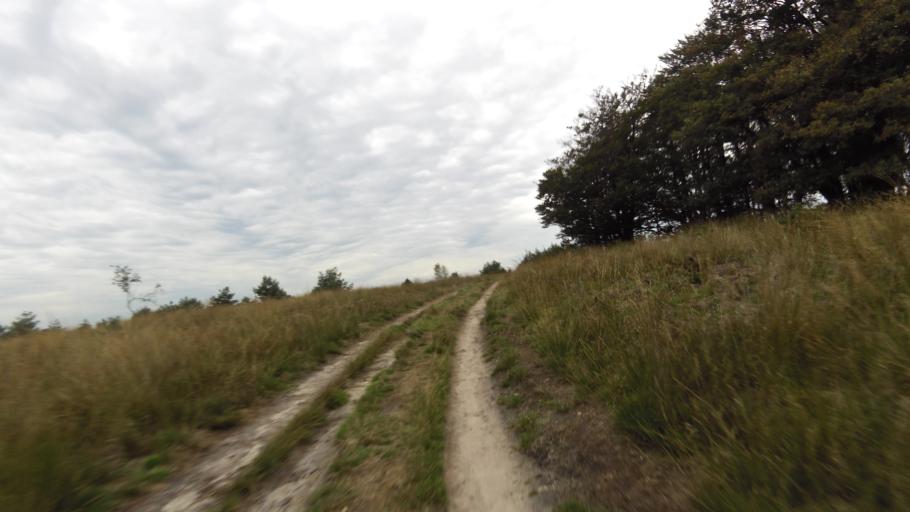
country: NL
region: Gelderland
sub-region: Gemeente Apeldoorn
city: Beekbergen
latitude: 52.1639
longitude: 5.8625
